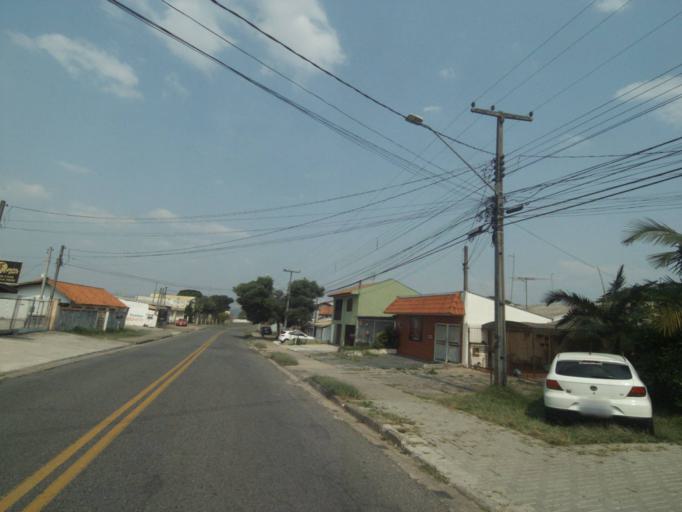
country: BR
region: Parana
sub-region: Sao Jose Dos Pinhais
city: Sao Jose dos Pinhais
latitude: -25.5321
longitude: -49.2412
